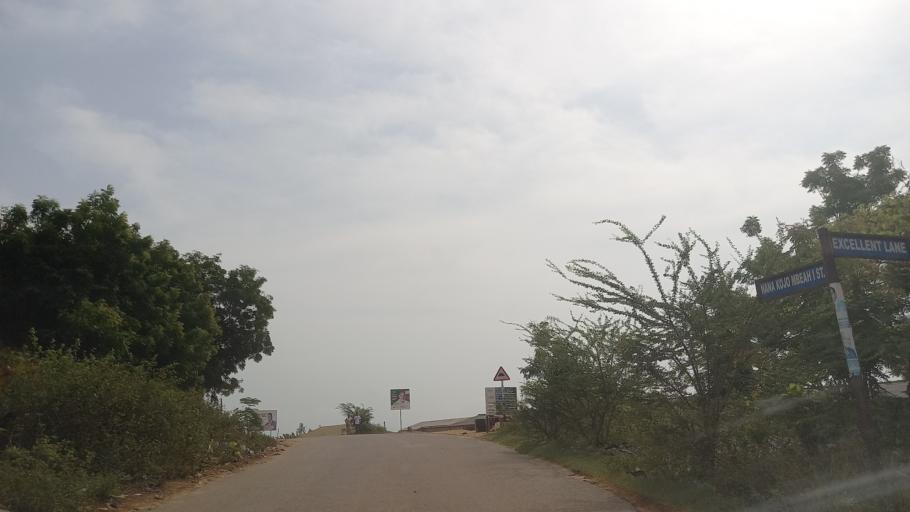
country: GH
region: Western
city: Shama Junction
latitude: 4.9774
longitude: -1.6451
